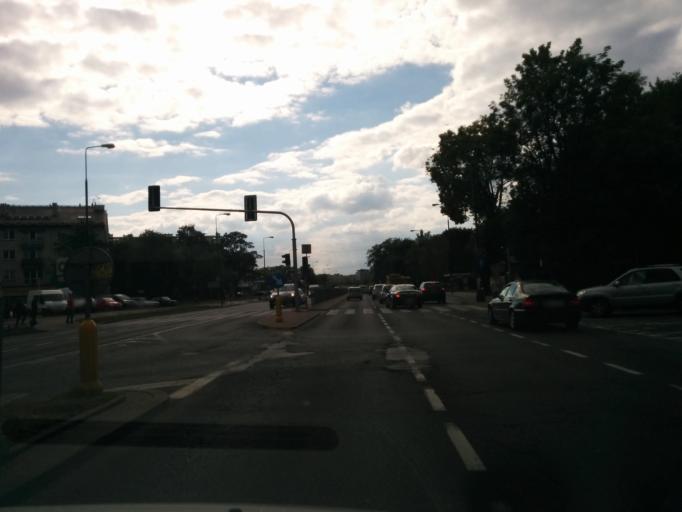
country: PL
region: Masovian Voivodeship
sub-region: Warszawa
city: Bemowo
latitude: 52.2399
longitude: 20.9359
